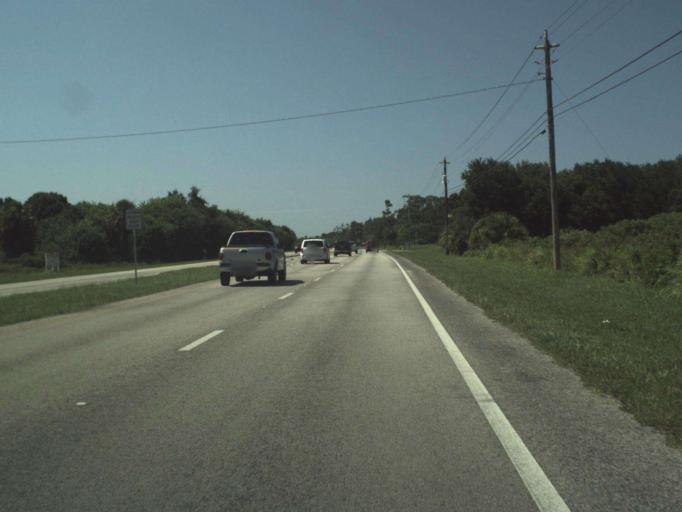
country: US
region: Florida
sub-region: Indian River County
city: Winter Beach
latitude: 27.7245
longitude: -80.4227
